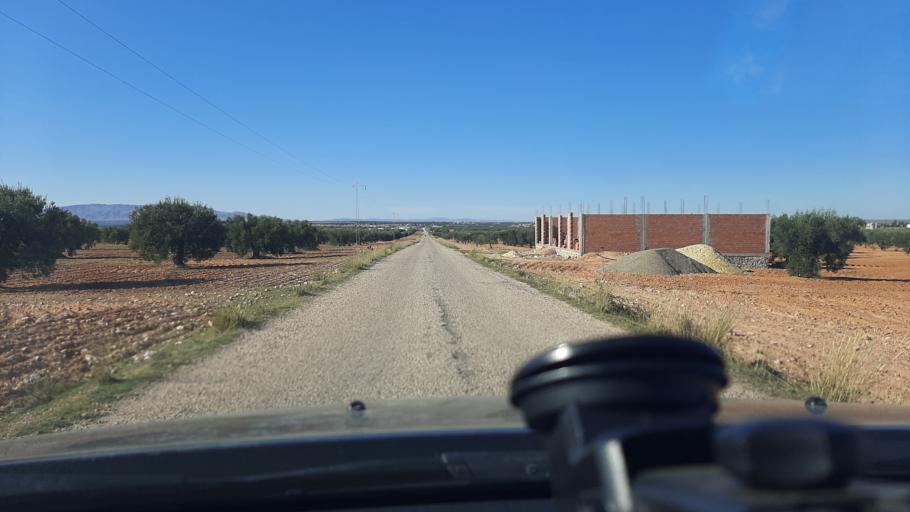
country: TN
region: Safaqis
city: Bi'r `Ali Bin Khalifah
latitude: 35.0082
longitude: 10.0887
